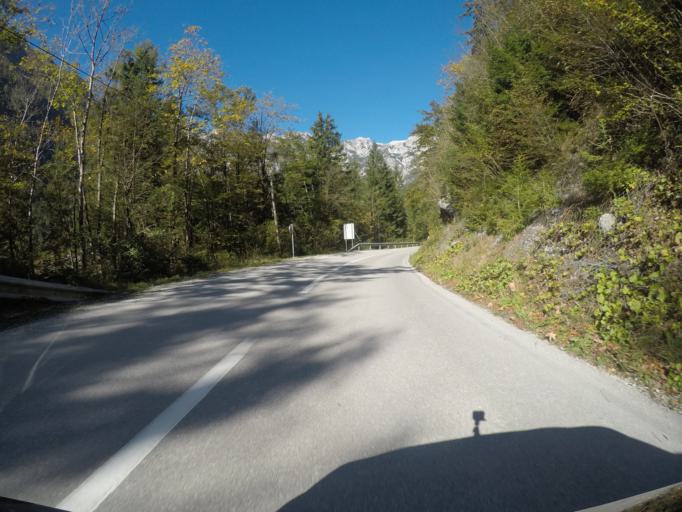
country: SI
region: Kamnik
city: Mekinje
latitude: 46.3250
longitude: 14.5922
